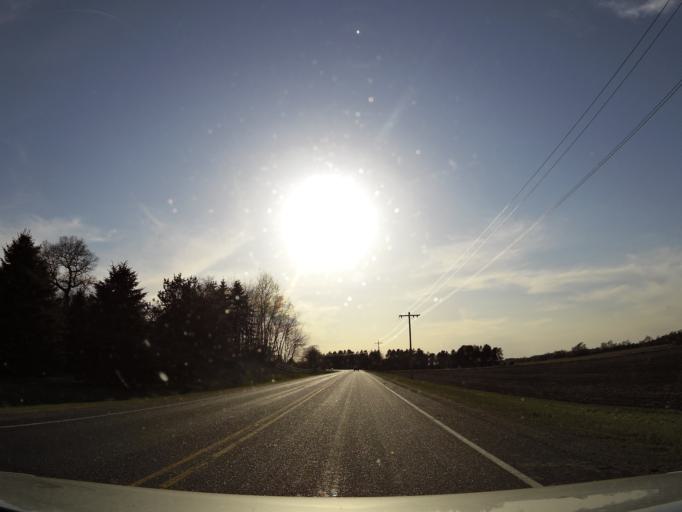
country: US
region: Wisconsin
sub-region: Pierce County
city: River Falls
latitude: 44.8258
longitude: -92.6875
